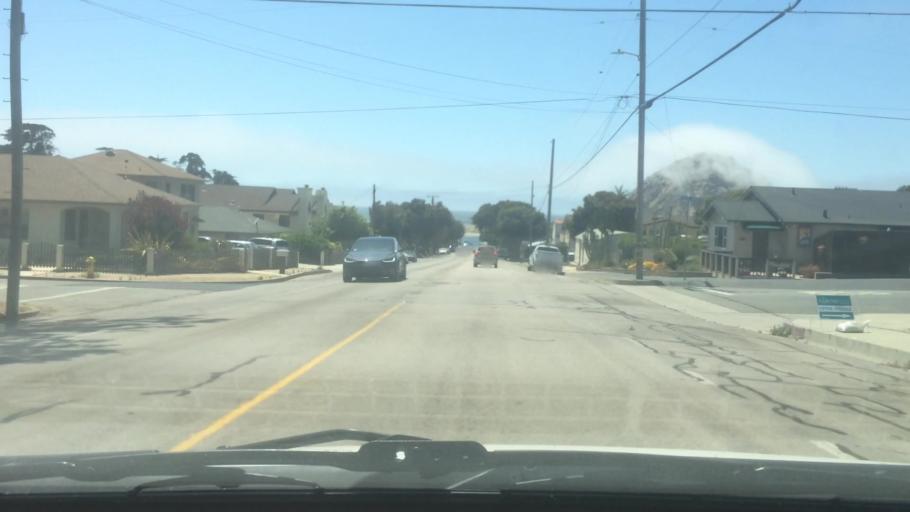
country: US
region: California
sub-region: San Luis Obispo County
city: Morro Bay
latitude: 35.3651
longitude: -120.8463
